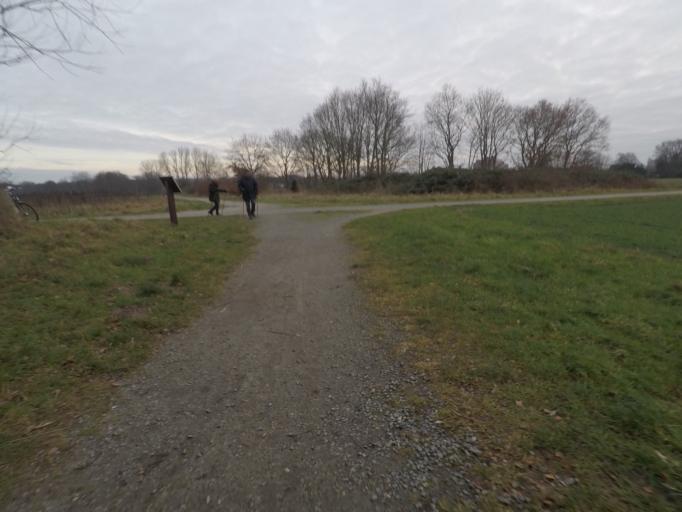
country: DE
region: Lower Saxony
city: Langen
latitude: 53.6029
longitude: 8.6011
